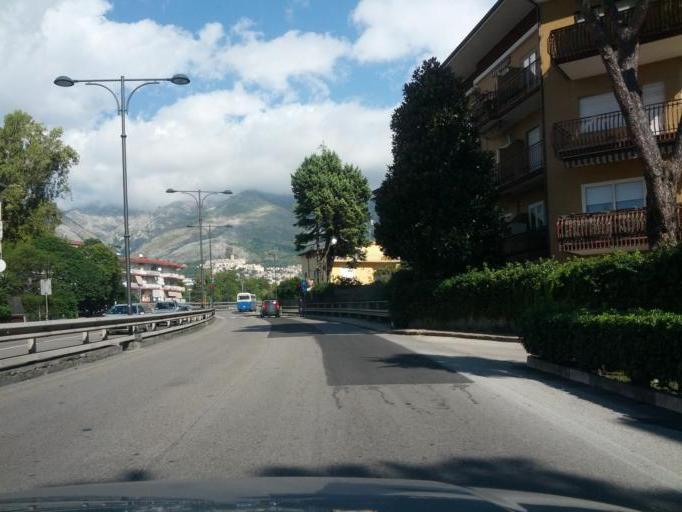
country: IT
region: Latium
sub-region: Provincia di Latina
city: Formia
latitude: 41.2628
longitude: 13.6205
